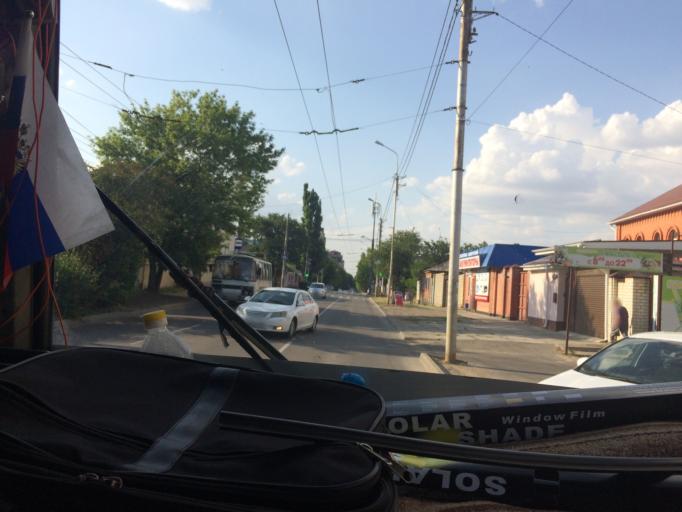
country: RU
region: Stavropol'skiy
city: Stavropol'
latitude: 45.0278
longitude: 41.9534
